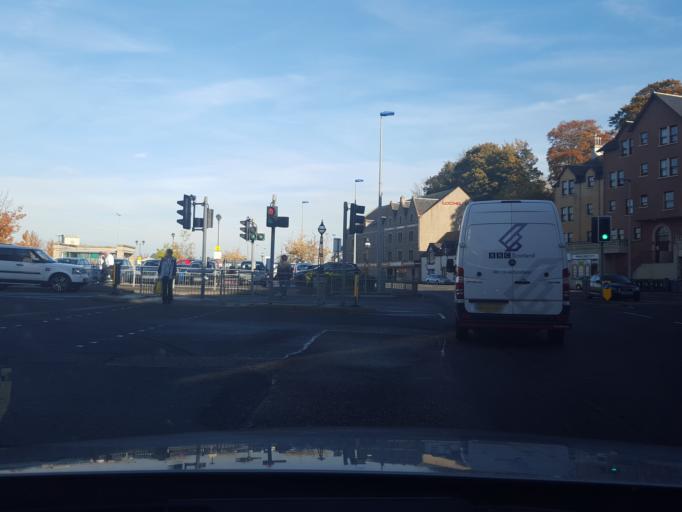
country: GB
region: Scotland
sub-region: Highland
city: Inverness
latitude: 57.4796
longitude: -4.2197
